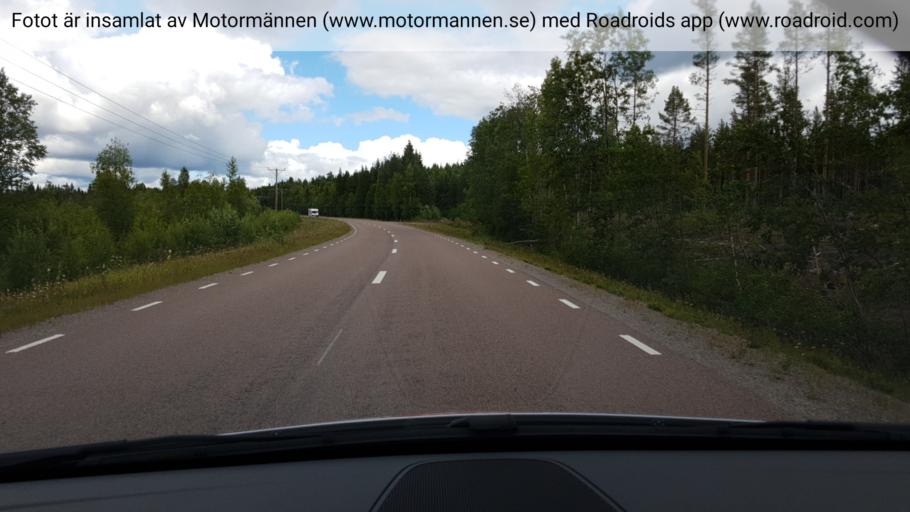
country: SE
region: Jaemtland
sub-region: Braecke Kommun
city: Braecke
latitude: 62.9163
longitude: 15.6780
